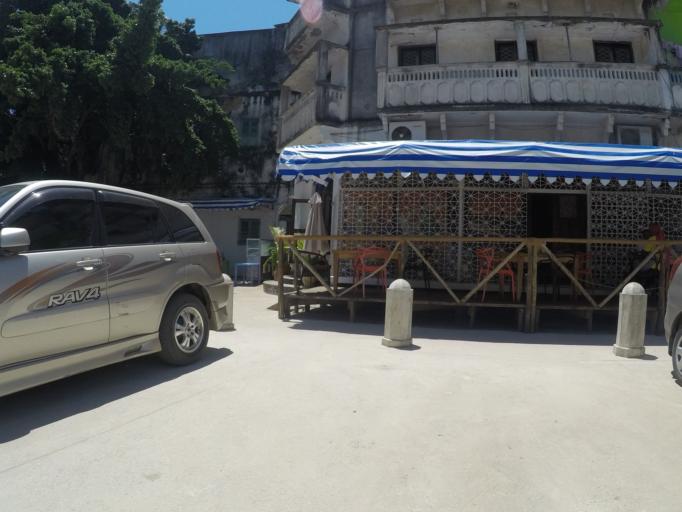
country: TZ
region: Zanzibar Urban/West
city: Zanzibar
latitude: -6.1587
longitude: 39.1921
